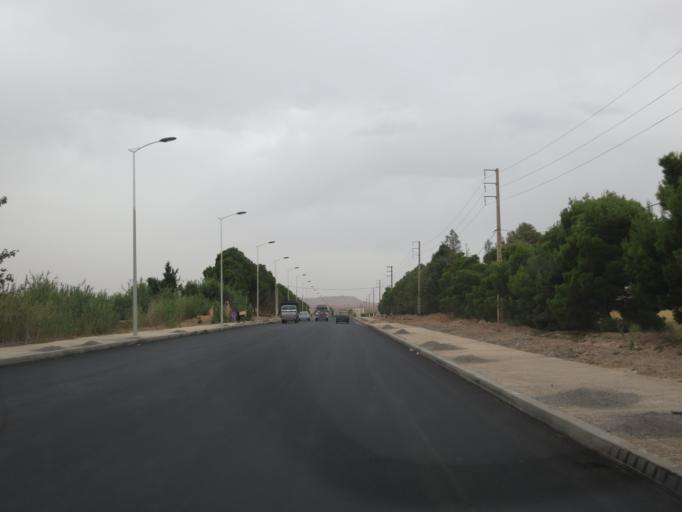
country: MA
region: Meknes-Tafilalet
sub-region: Khenifra
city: Midelt
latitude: 32.7064
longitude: -4.7939
